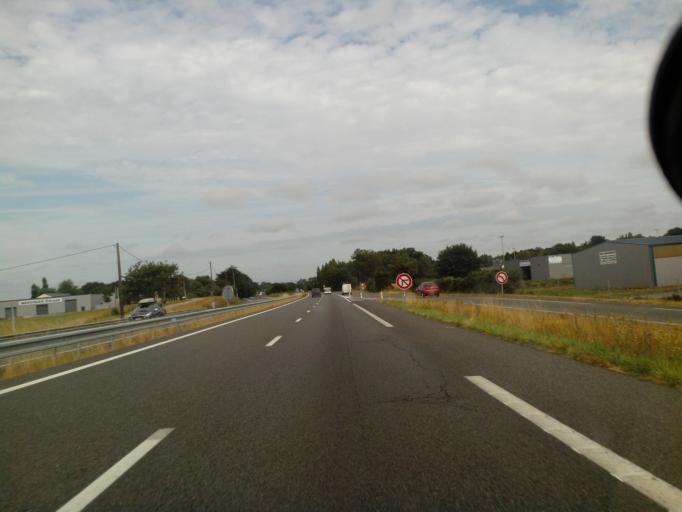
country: FR
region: Brittany
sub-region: Departement du Morbihan
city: Muzillac
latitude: 47.5597
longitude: -2.5016
